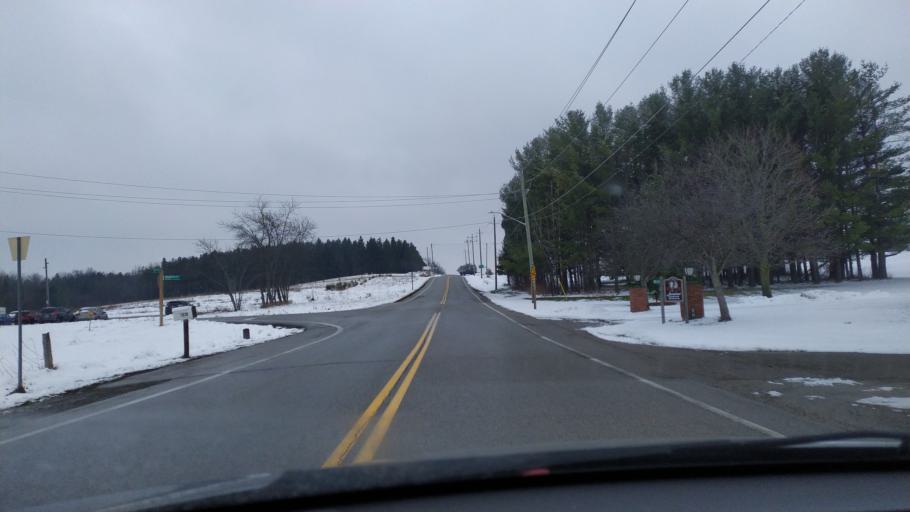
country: CA
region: Ontario
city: Waterloo
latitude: 43.4860
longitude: -80.6251
